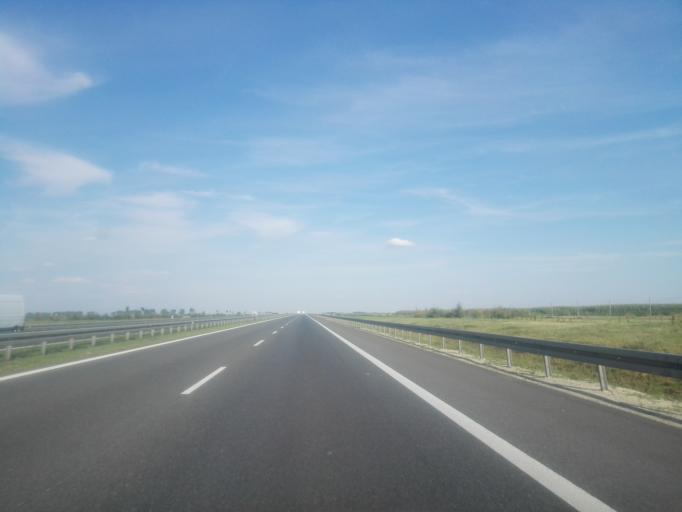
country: PL
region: Lower Silesian Voivodeship
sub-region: Powiat olesnicki
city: Dobroszyce
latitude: 51.2264
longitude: 17.2749
